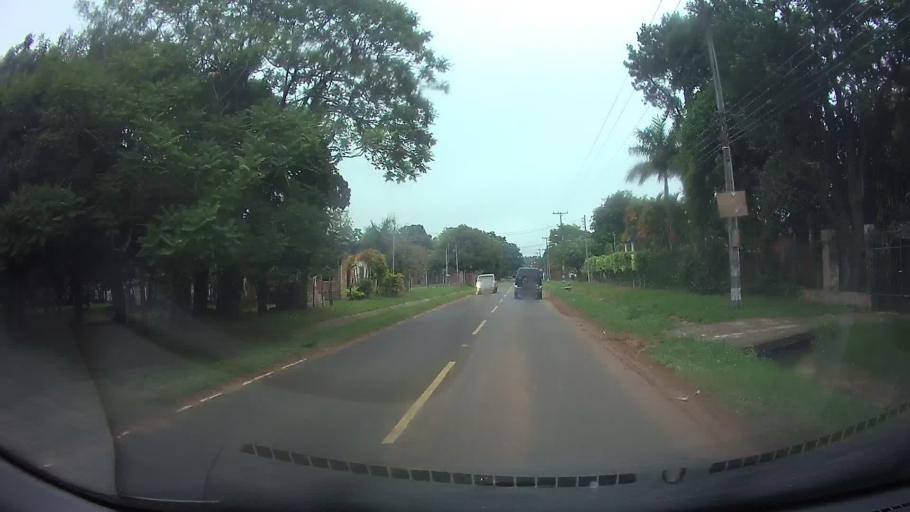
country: PY
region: Central
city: Itaugua
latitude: -25.3519
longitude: -57.3387
